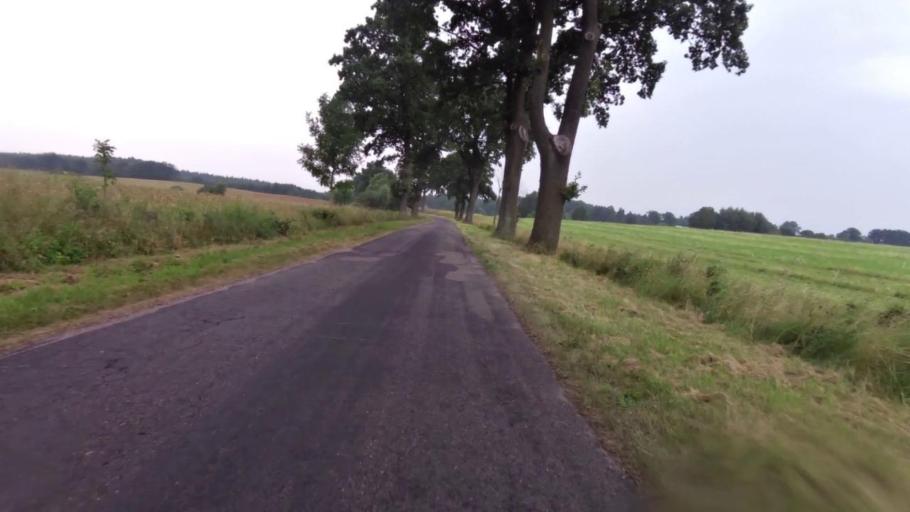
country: PL
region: West Pomeranian Voivodeship
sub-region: Powiat lobeski
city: Wegorzyno
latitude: 53.5101
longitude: 15.6492
